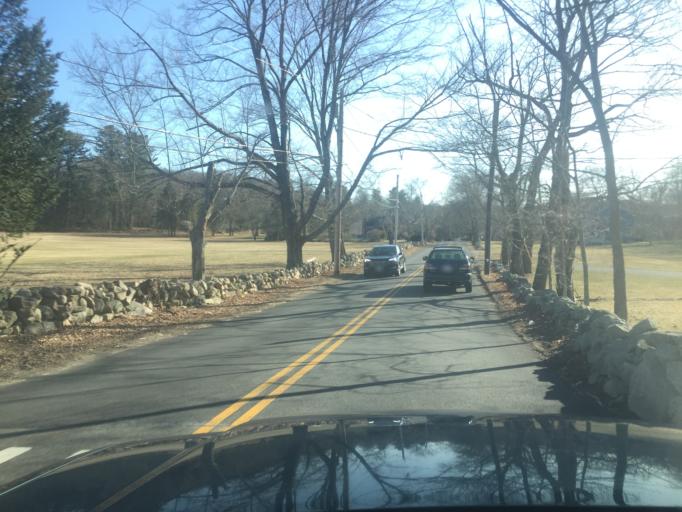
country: US
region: Massachusetts
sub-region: Norfolk County
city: Norfolk
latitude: 42.1131
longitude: -71.3569
